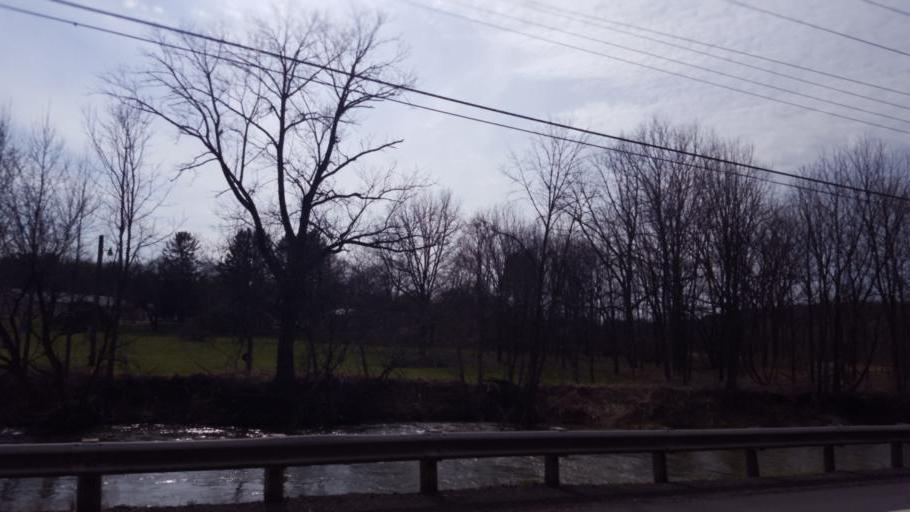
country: US
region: Ohio
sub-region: Sandusky County
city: Bellville
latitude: 40.6253
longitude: -82.5127
